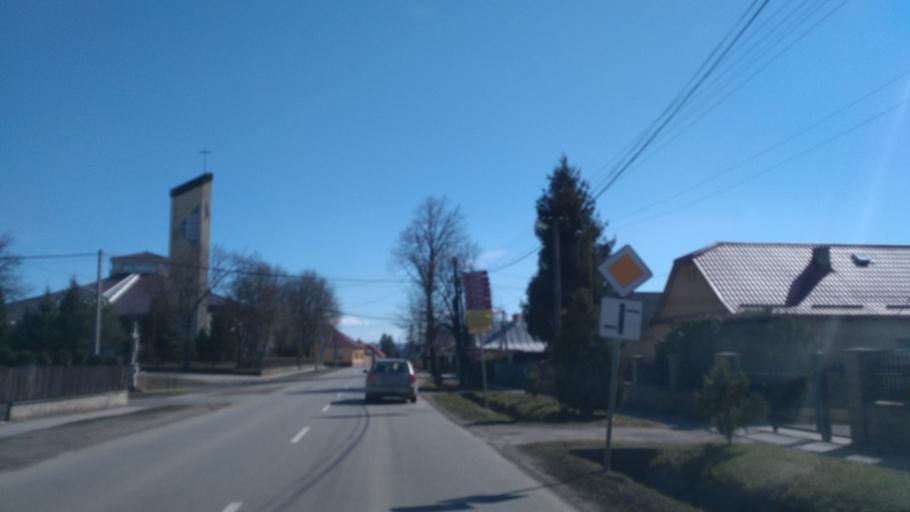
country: SK
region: Kosicky
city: Kosice
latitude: 48.6278
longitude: 21.3066
